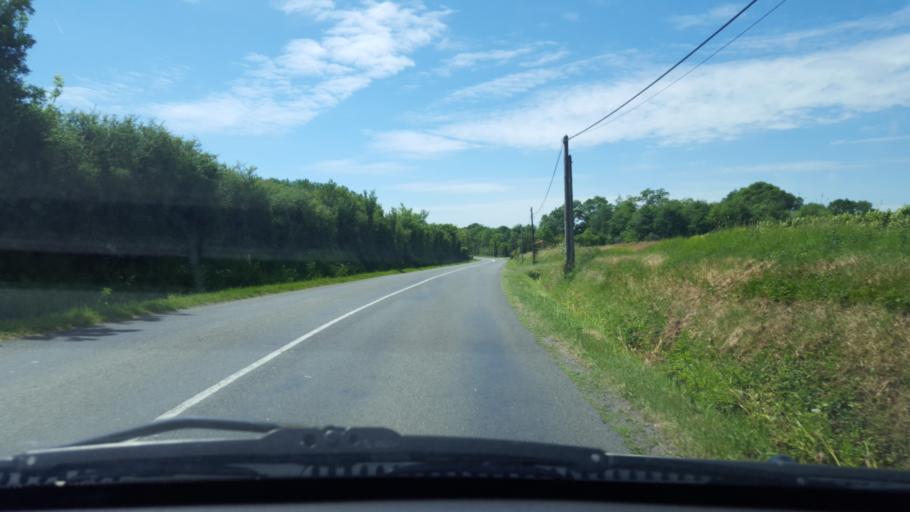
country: FR
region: Pays de la Loire
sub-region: Departement de la Loire-Atlantique
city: Saint-Philbert-de-Grand-Lieu
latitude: 47.0082
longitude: -1.6552
